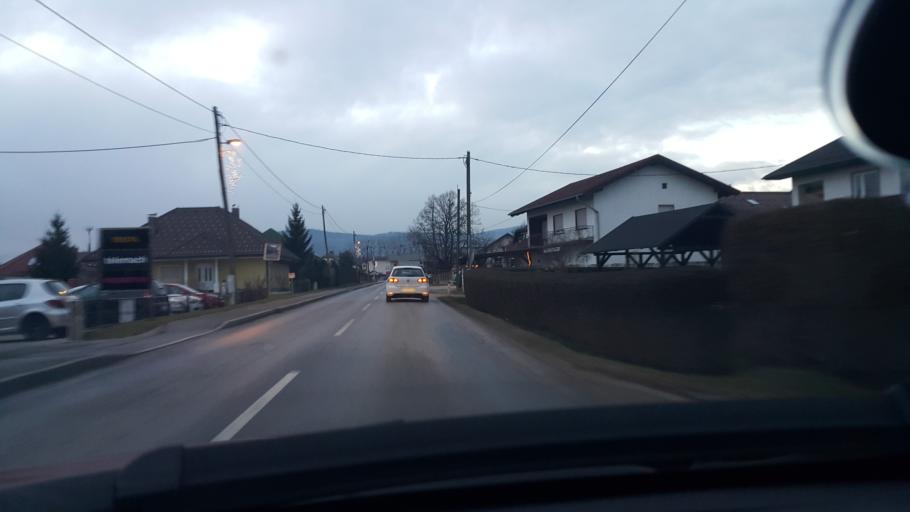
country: SI
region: Hoce-Slivnica
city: Hotinja Vas
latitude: 46.4527
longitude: 15.6609
